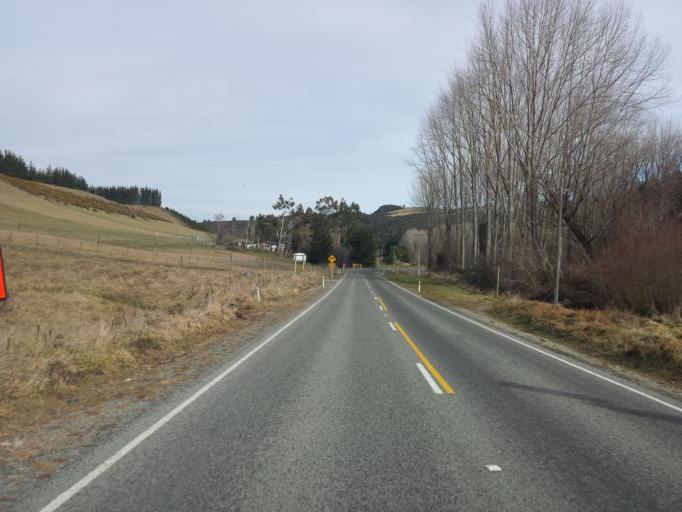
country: NZ
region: Canterbury
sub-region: Timaru District
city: Pleasant Point
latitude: -44.1280
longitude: 171.0915
